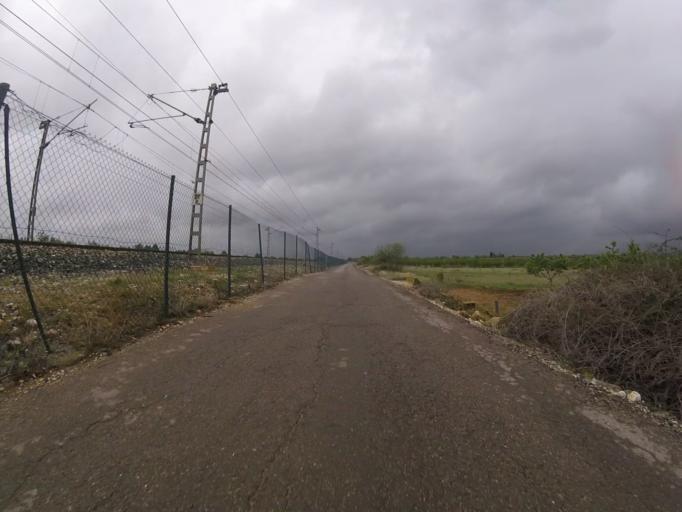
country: ES
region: Valencia
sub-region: Provincia de Castello
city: Alcala de Xivert
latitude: 40.2932
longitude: 0.2243
